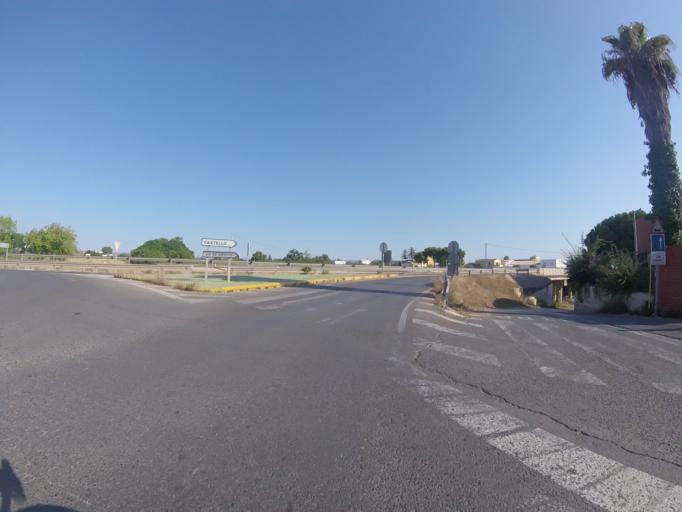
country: ES
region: Valencia
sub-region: Provincia de Castello
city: Benicarlo
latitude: 40.4238
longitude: 0.4308
